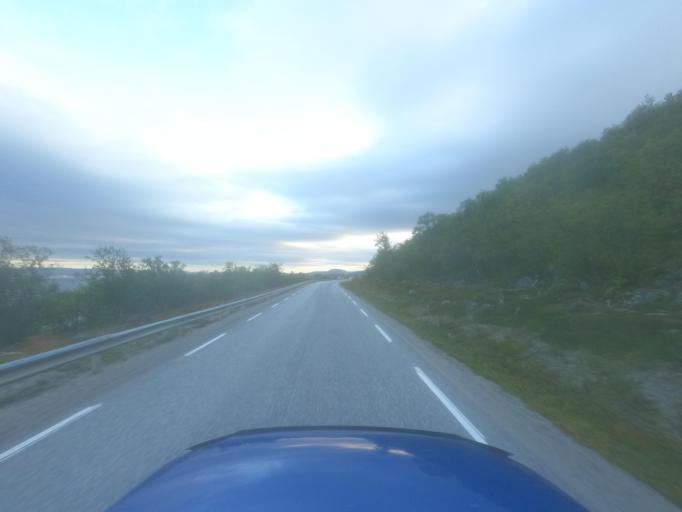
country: NO
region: Finnmark Fylke
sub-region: Porsanger
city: Lakselv
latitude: 70.4008
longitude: 25.1361
